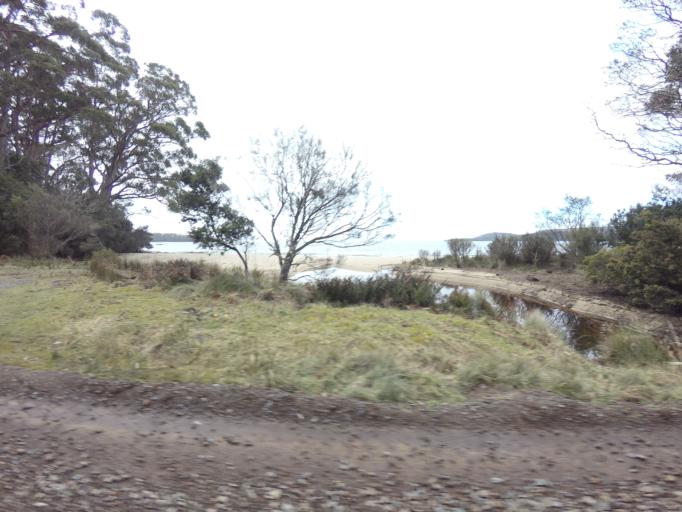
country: AU
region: Tasmania
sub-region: Huon Valley
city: Geeveston
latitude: -43.5423
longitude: 146.8920
